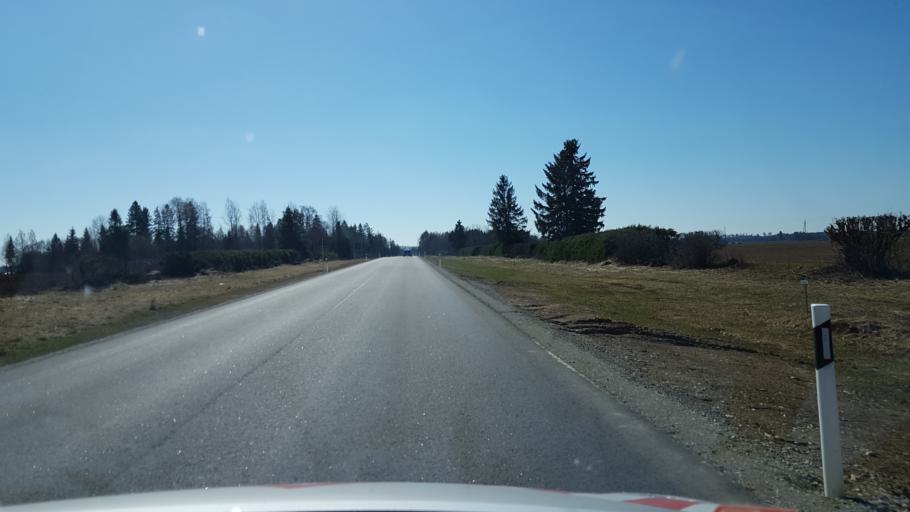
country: EE
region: Laeaene-Virumaa
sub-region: Vinni vald
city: Vinni
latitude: 59.0713
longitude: 26.6363
